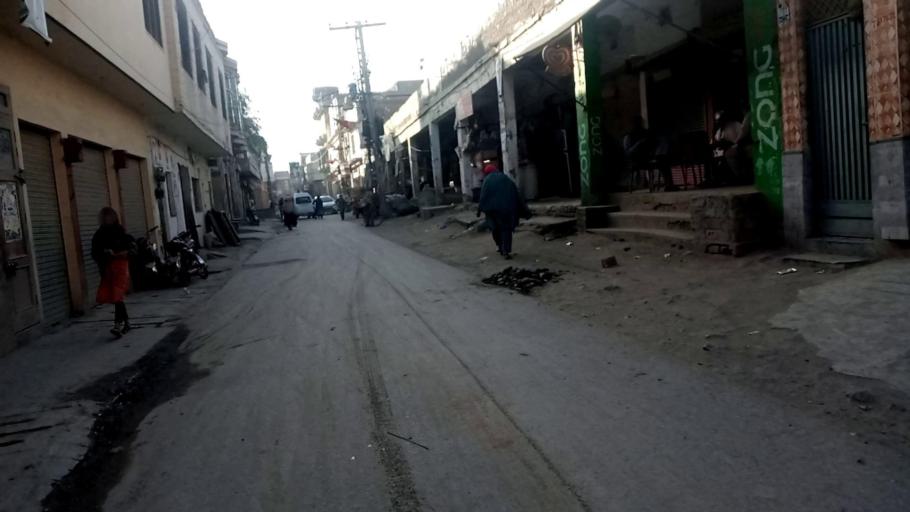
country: PK
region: Khyber Pakhtunkhwa
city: Peshawar
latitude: 34.0059
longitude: 71.6005
